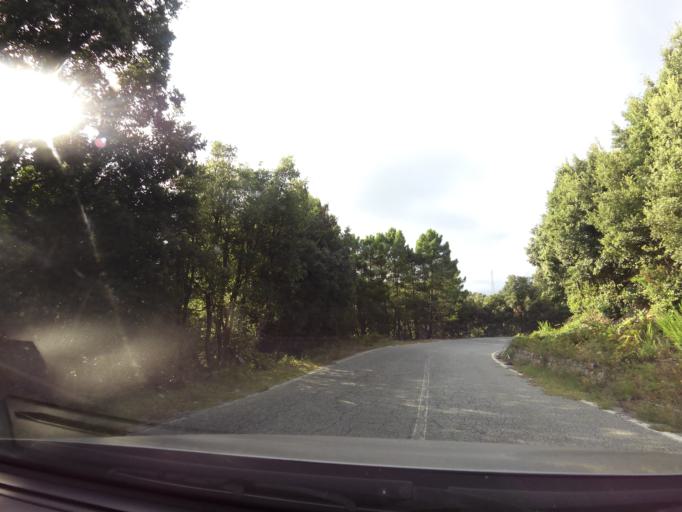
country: IT
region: Calabria
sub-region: Provincia di Vibo-Valentia
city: Nardodipace
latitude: 38.4779
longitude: 16.3828
